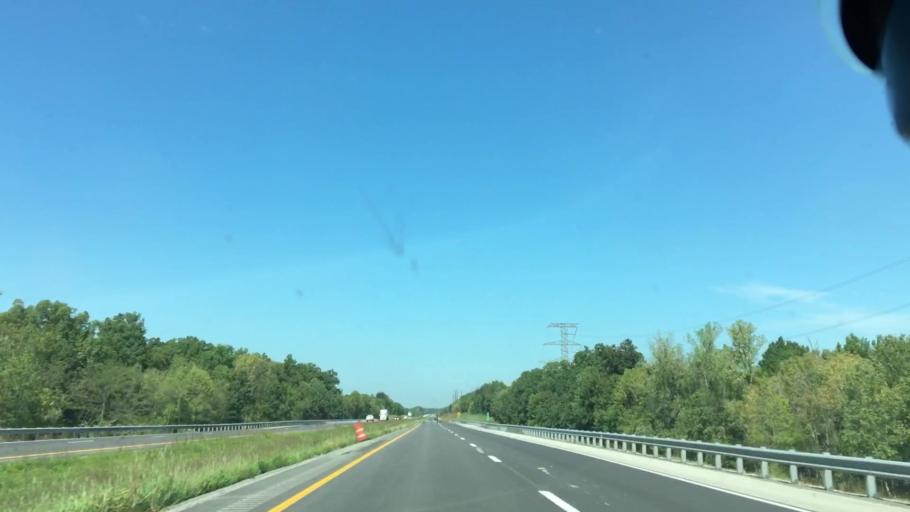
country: US
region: Kentucky
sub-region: Webster County
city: Sebree
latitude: 37.6290
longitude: -87.5084
